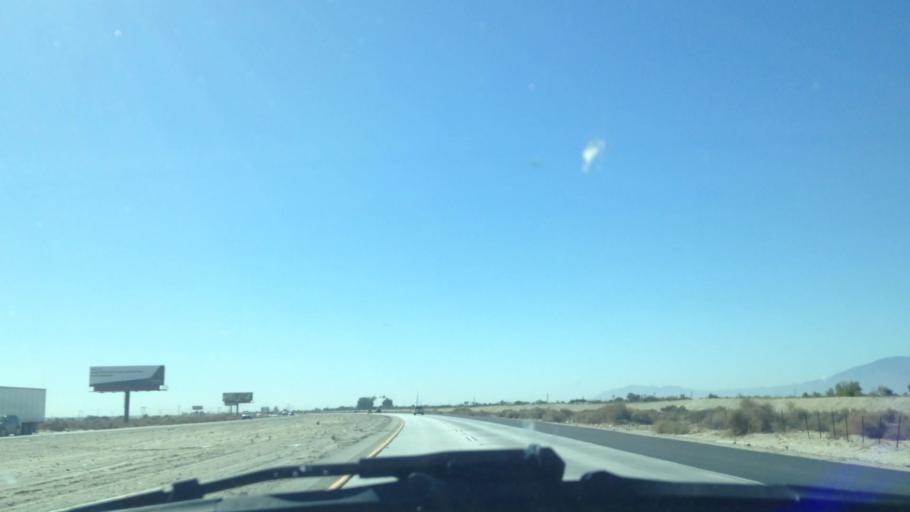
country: US
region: California
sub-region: Riverside County
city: Coachella
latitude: 33.6970
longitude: -116.1733
